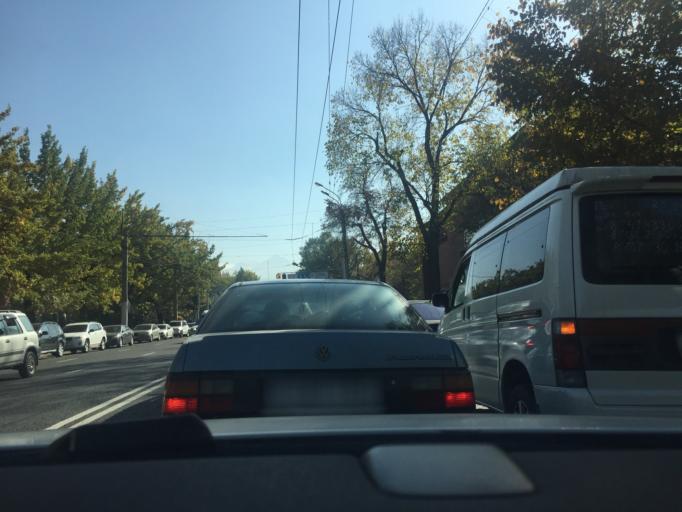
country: KZ
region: Almaty Qalasy
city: Almaty
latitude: 43.2407
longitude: 76.9038
